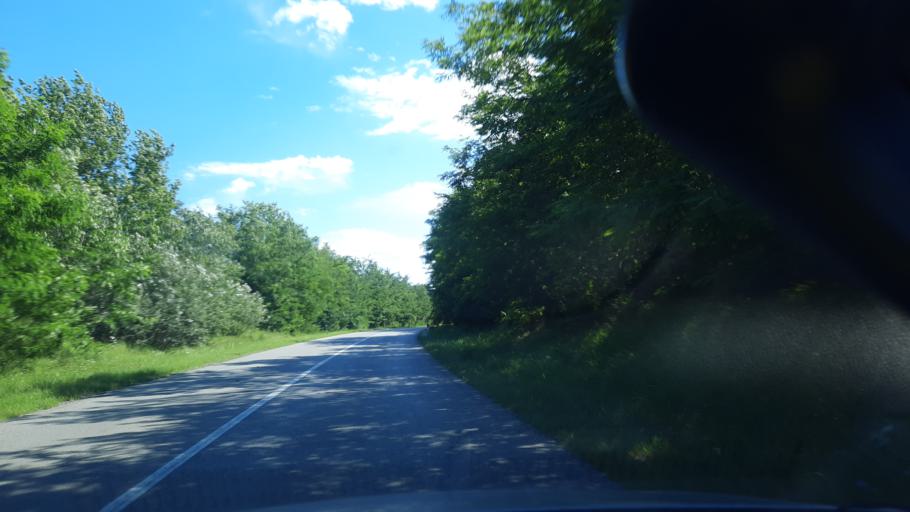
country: RO
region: Caras-Severin
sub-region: Comuna Socol
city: Socol
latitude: 44.8676
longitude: 21.3122
